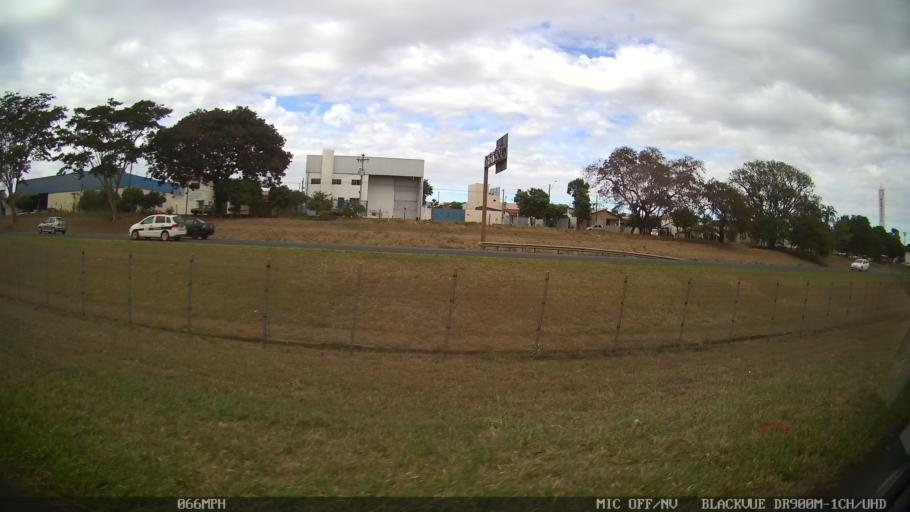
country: BR
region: Sao Paulo
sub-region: Bady Bassitt
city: Bady Bassitt
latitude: -20.8070
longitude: -49.5118
